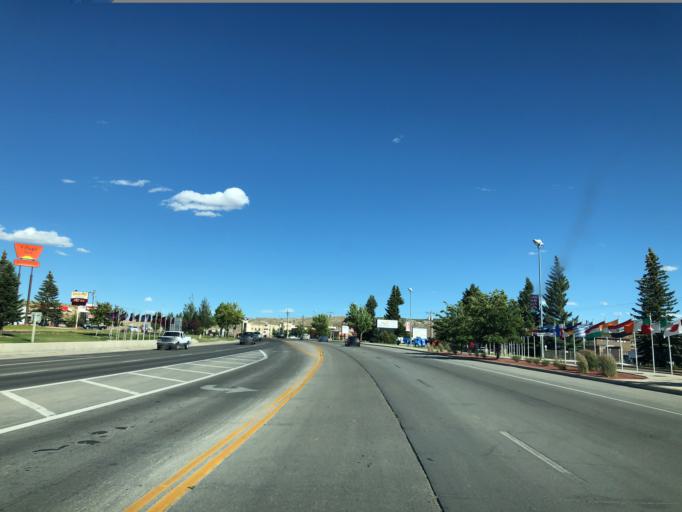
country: US
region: Wyoming
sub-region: Sweetwater County
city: Rock Springs
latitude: 41.5761
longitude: -109.2502
